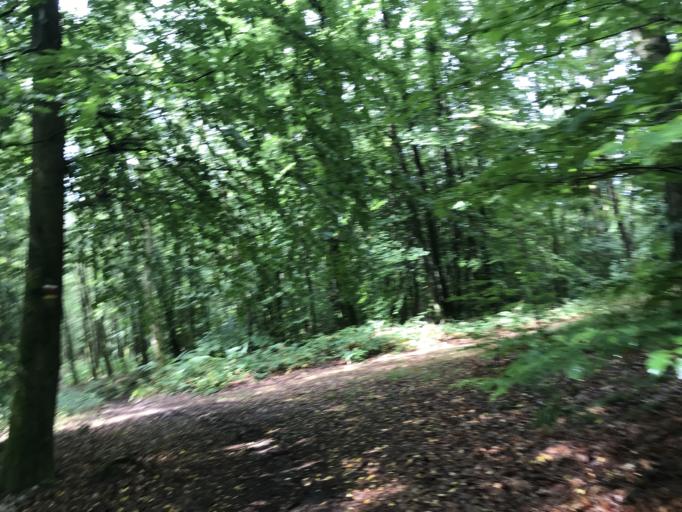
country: FR
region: Champagne-Ardenne
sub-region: Departement des Ardennes
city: Thilay
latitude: 49.8841
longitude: 4.7839
